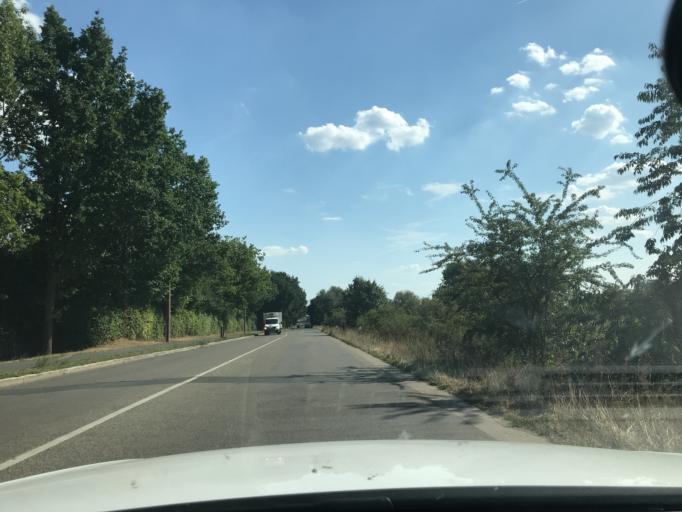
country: DE
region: Bavaria
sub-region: Regierungsbezirk Mittelfranken
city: Erlangen
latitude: 49.5678
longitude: 10.9848
